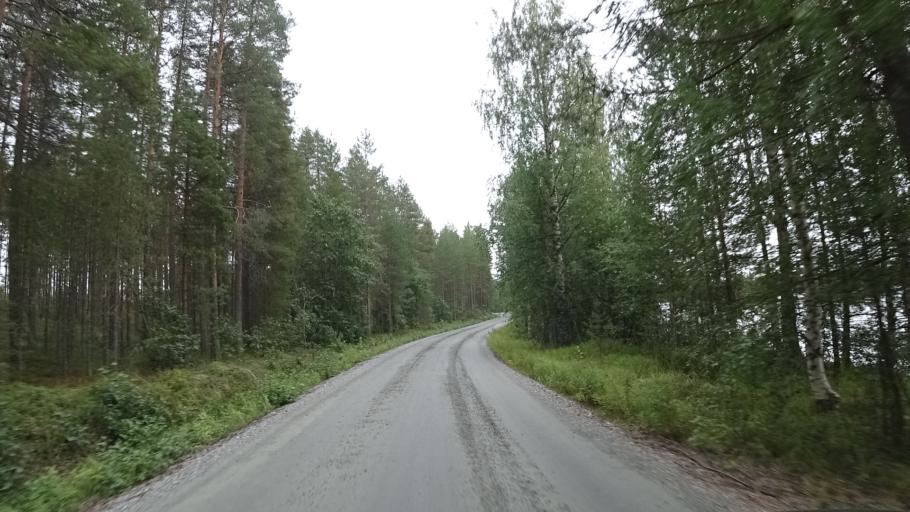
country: FI
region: North Karelia
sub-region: Pielisen Karjala
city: Lieksa
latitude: 63.3827
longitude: 30.3413
